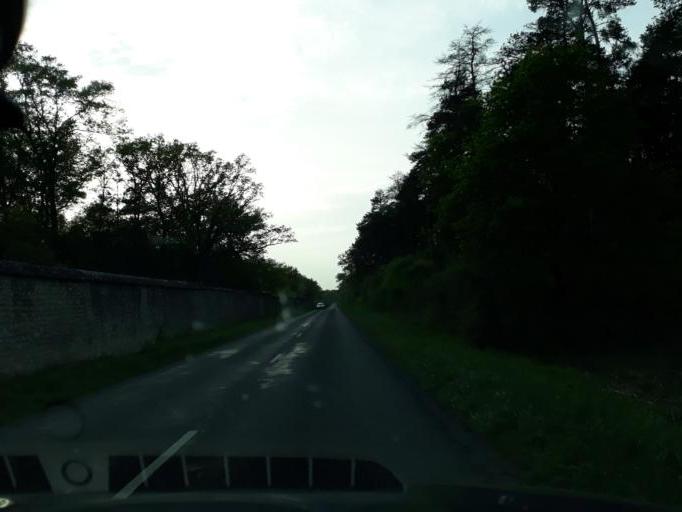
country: FR
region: Centre
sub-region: Departement du Loir-et-Cher
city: Muides-sur-Loire
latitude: 47.6535
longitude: 1.5626
